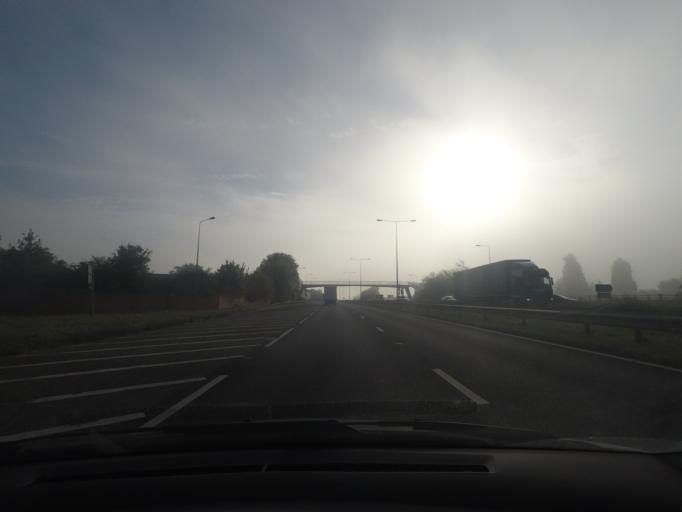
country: GB
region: England
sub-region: East Riding of Yorkshire
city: Welton
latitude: 53.7318
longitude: -0.5530
